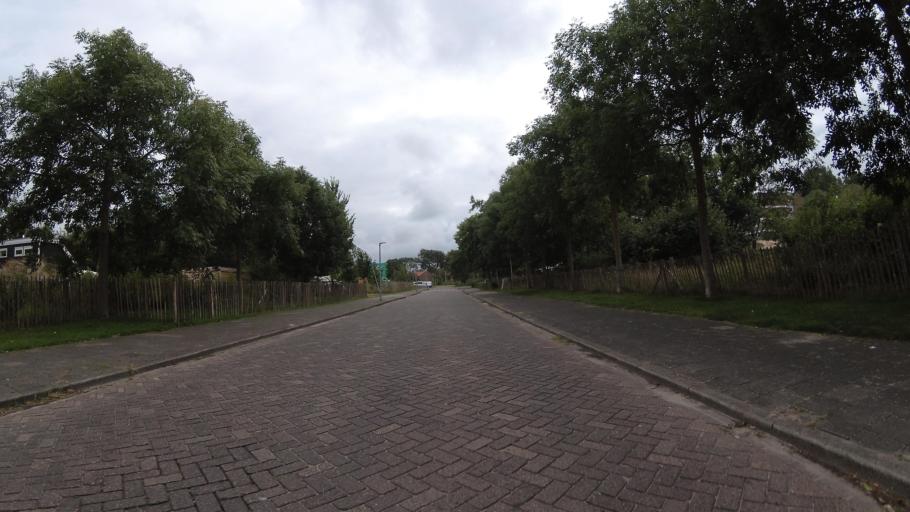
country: NL
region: North Holland
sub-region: Gemeente Den Helder
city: Den Helder
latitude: 52.9403
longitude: 4.7431
